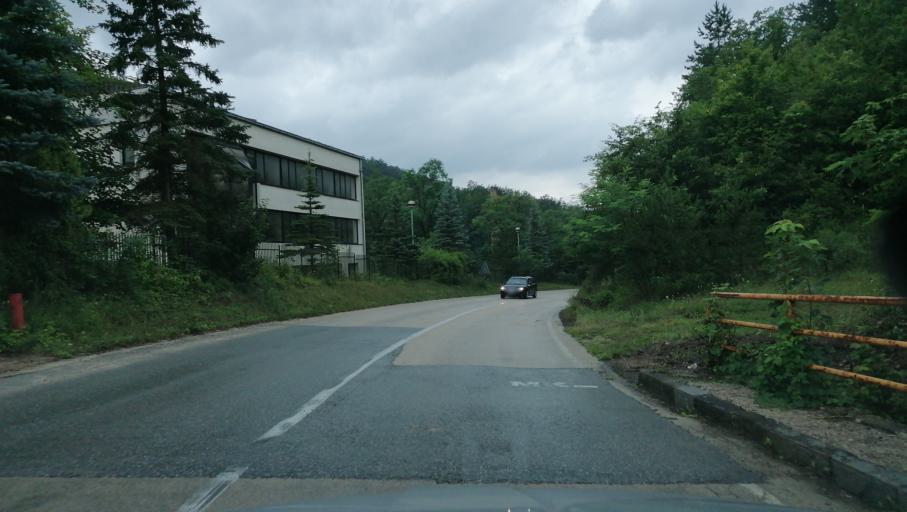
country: RS
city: Durici
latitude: 43.7790
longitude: 19.4813
